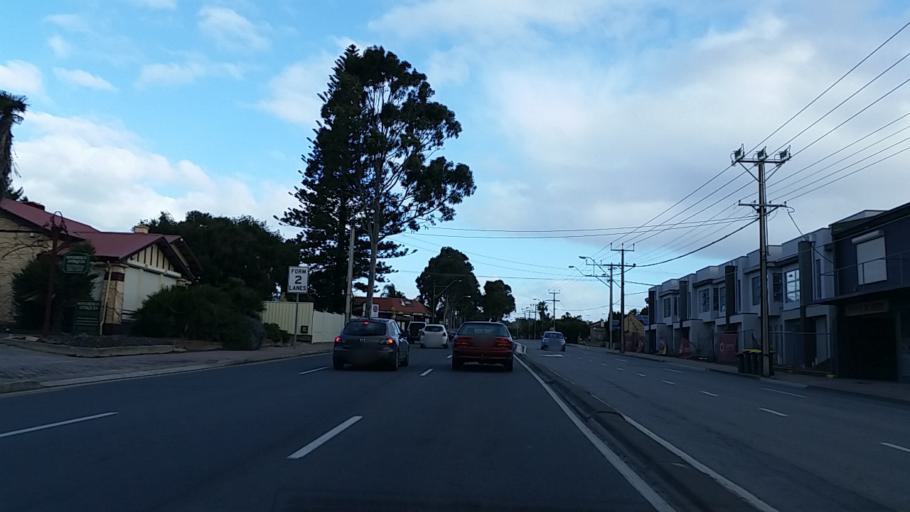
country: AU
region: South Australia
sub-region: Adelaide Hills
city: Seacliff
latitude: -35.0305
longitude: 138.5240
